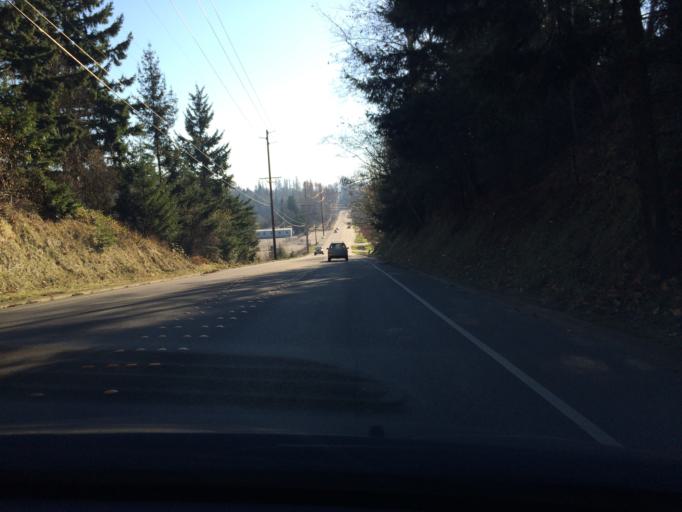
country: US
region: Washington
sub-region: Whatcom County
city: Bellingham
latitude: 48.7863
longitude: -122.4426
